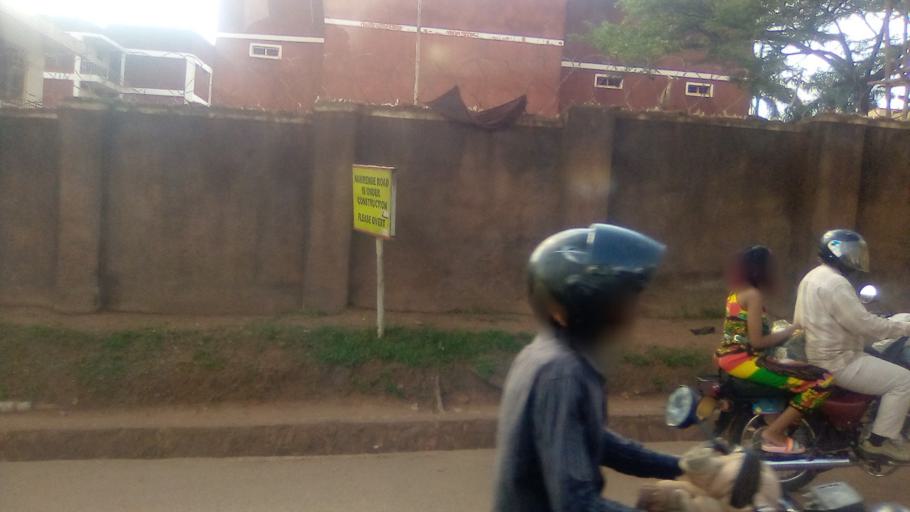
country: UG
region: Central Region
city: Kampala Central Division
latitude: 0.3122
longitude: 32.5689
